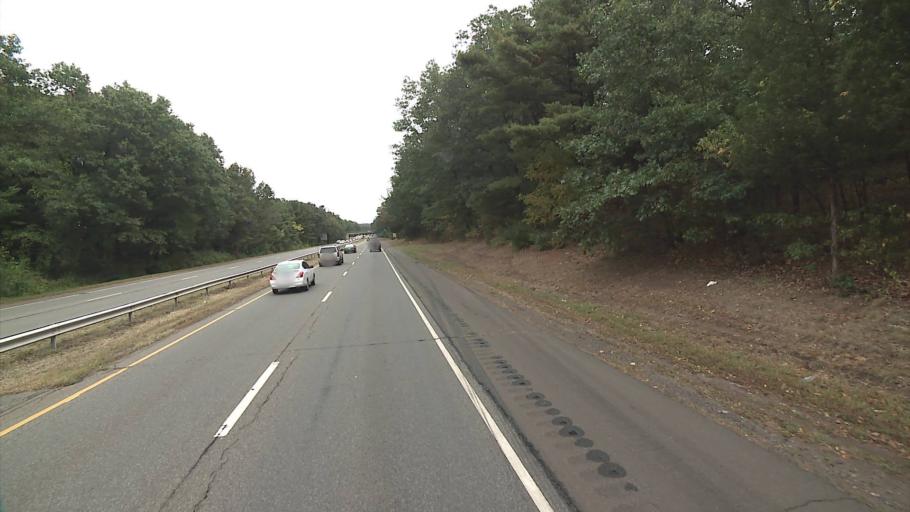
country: US
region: Connecticut
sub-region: New Haven County
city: Hamden
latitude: 41.3697
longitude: -72.9145
